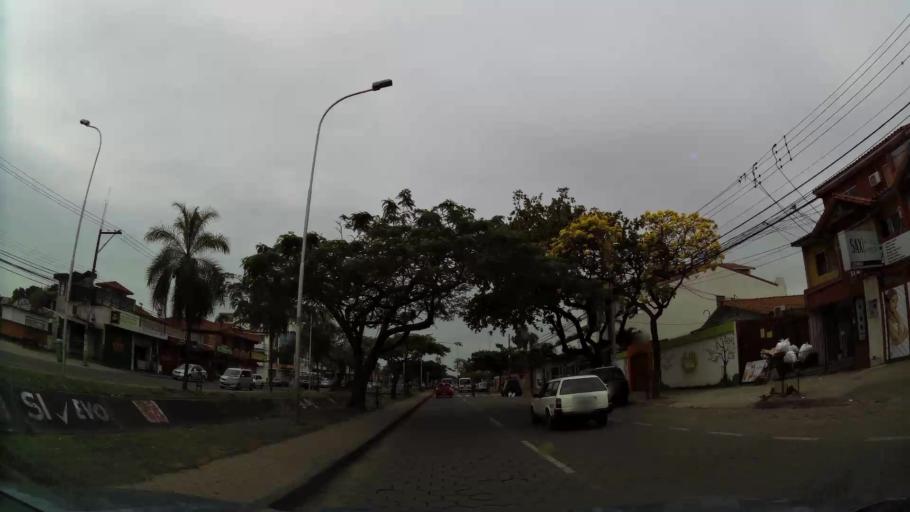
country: BO
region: Santa Cruz
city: Santa Cruz de la Sierra
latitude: -17.7917
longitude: -63.1982
